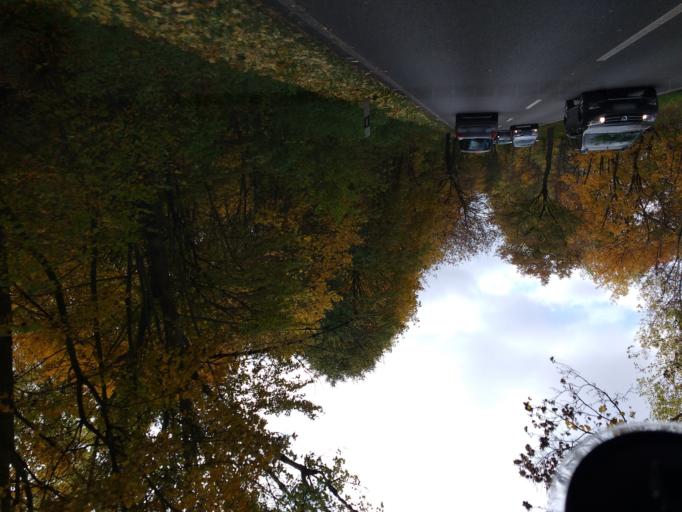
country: DE
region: Berlin
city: Hellersdorf
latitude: 52.5452
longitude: 13.6137
